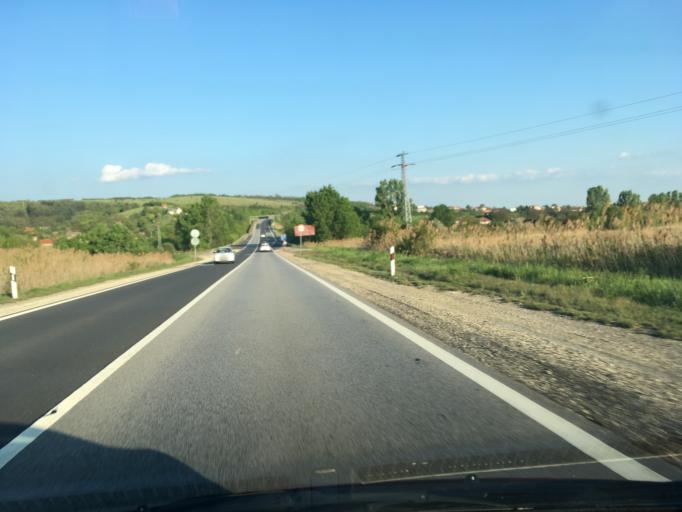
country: HU
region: Pest
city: Vac
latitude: 47.8089
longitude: 19.1229
